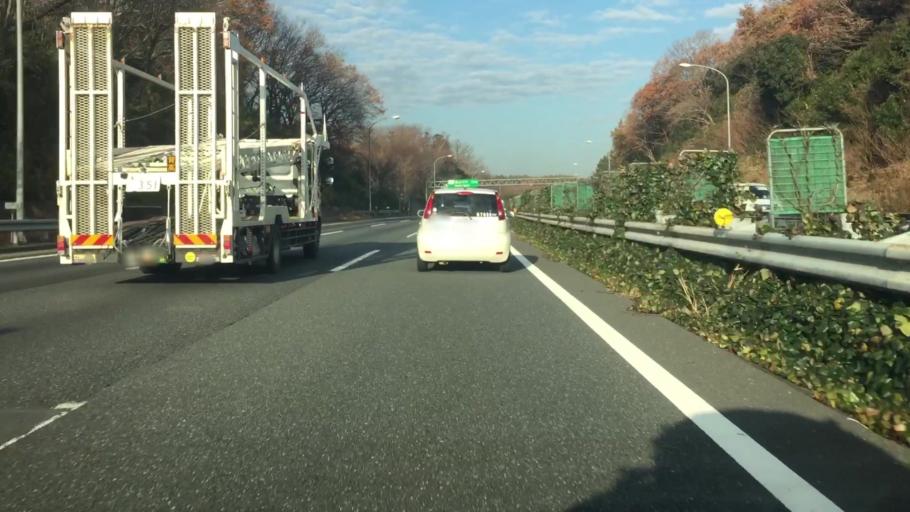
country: JP
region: Saitama
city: Ogawa
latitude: 36.0570
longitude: 139.3329
